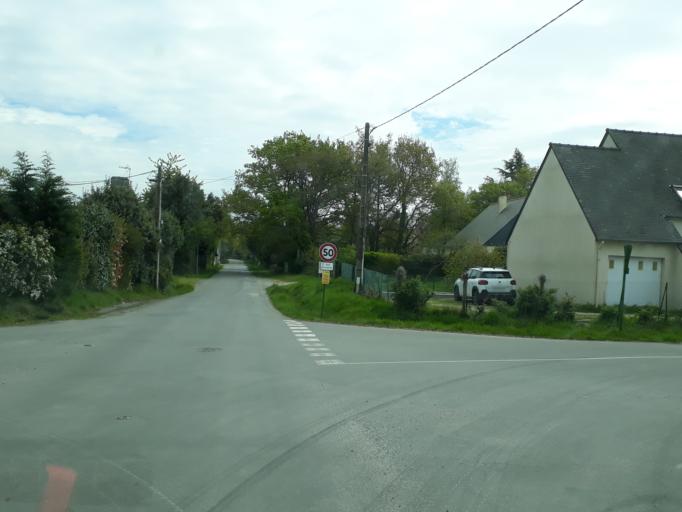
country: FR
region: Brittany
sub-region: Departement du Morbihan
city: Surzur
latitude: 47.5827
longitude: -2.6506
